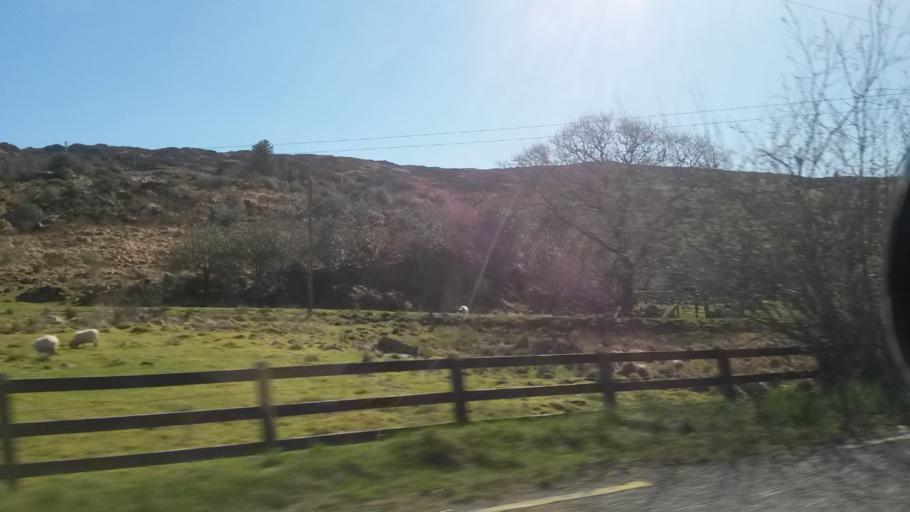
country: IE
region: Munster
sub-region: Ciarrai
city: Cill Airne
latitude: 51.9385
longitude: -9.3822
